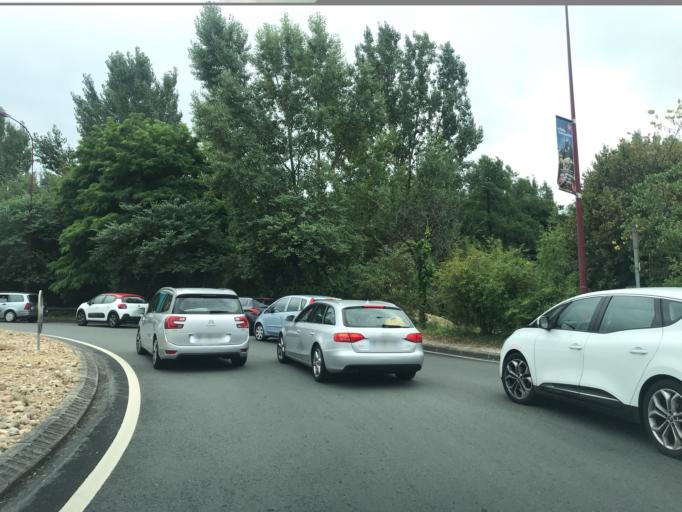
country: FR
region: Aquitaine
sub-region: Departement de la Dordogne
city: Chancelade
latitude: 45.2000
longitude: 0.6744
